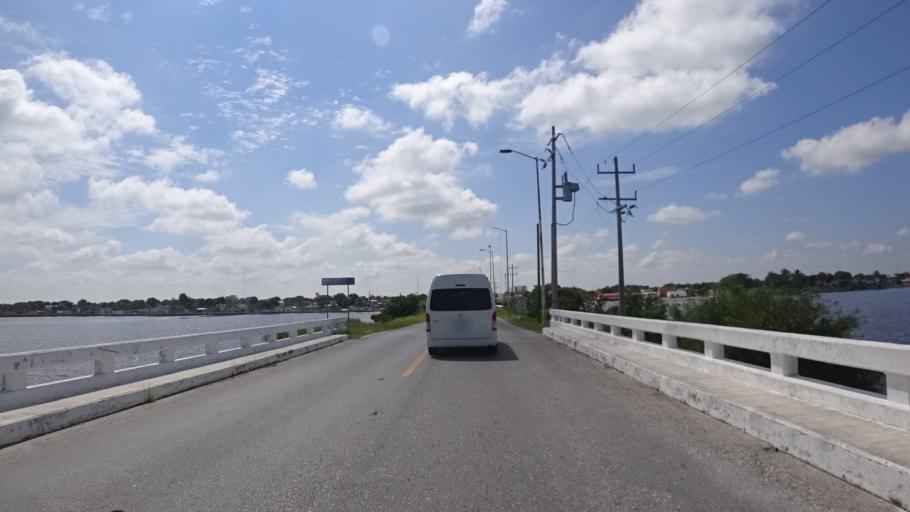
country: MX
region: Campeche
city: Sabancuy
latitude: 18.9779
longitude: -91.1820
